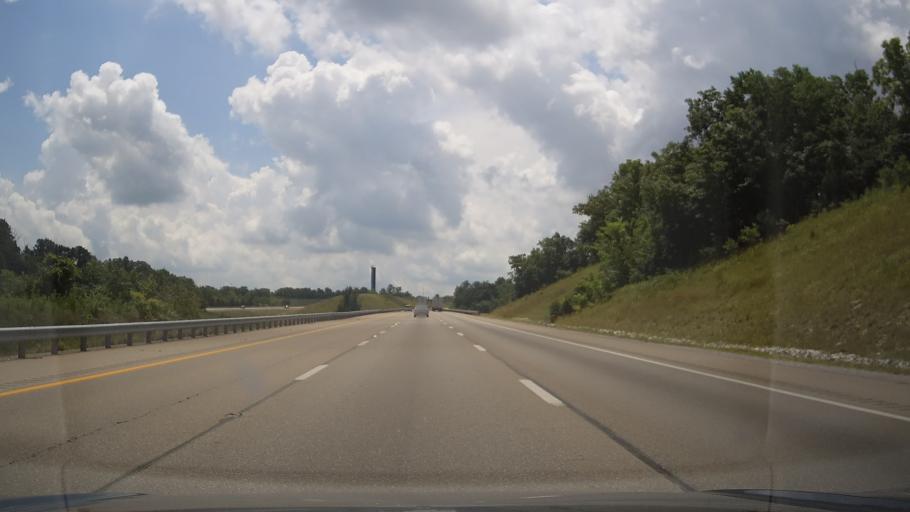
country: US
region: Kentucky
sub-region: Grant County
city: Williamstown
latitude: 38.5325
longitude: -84.5898
